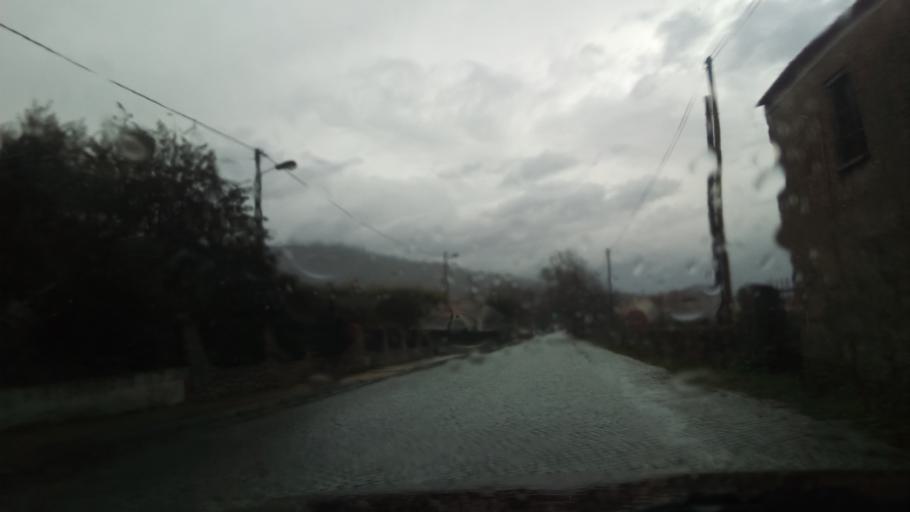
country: PT
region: Guarda
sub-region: Guarda
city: Guarda
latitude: 40.6017
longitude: -7.2939
